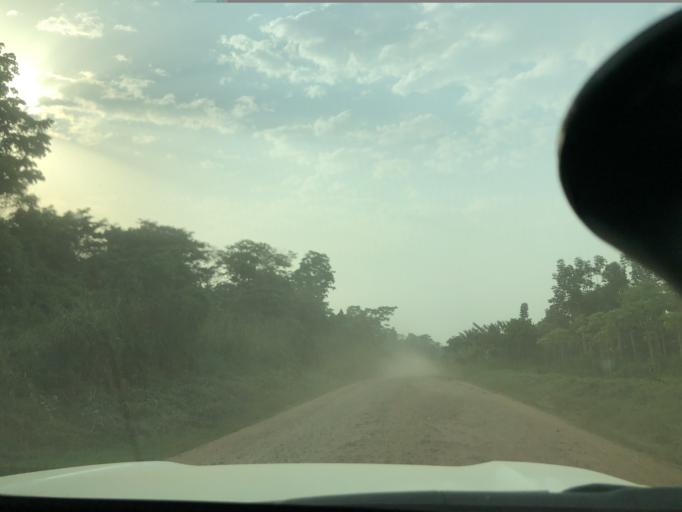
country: UG
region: Western Region
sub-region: Kasese District
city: Margherita
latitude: 0.2832
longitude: 29.6686
